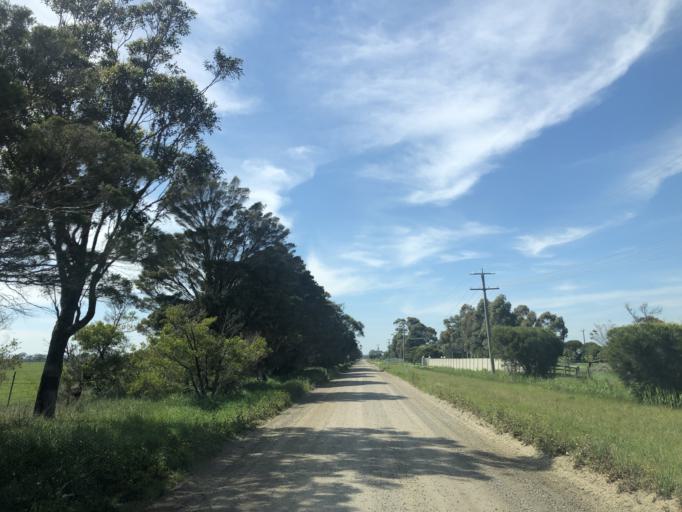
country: AU
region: Victoria
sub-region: Frankston
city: Sandhurst
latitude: -38.0560
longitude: 145.1873
